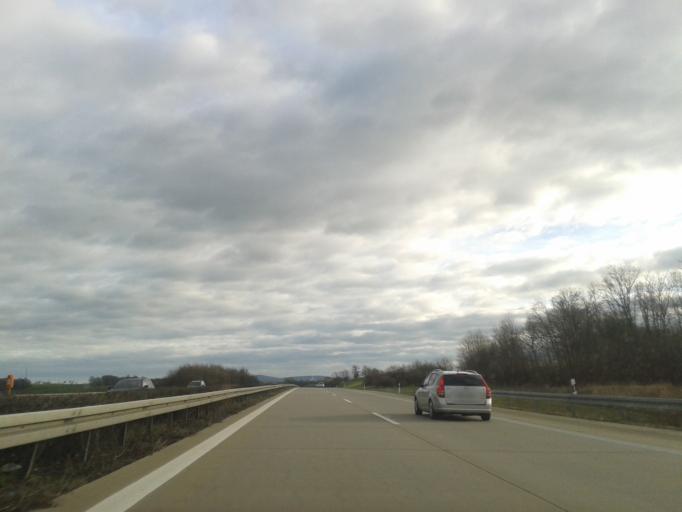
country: DE
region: Saxony
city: Weissenberg
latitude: 51.2089
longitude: 14.6377
